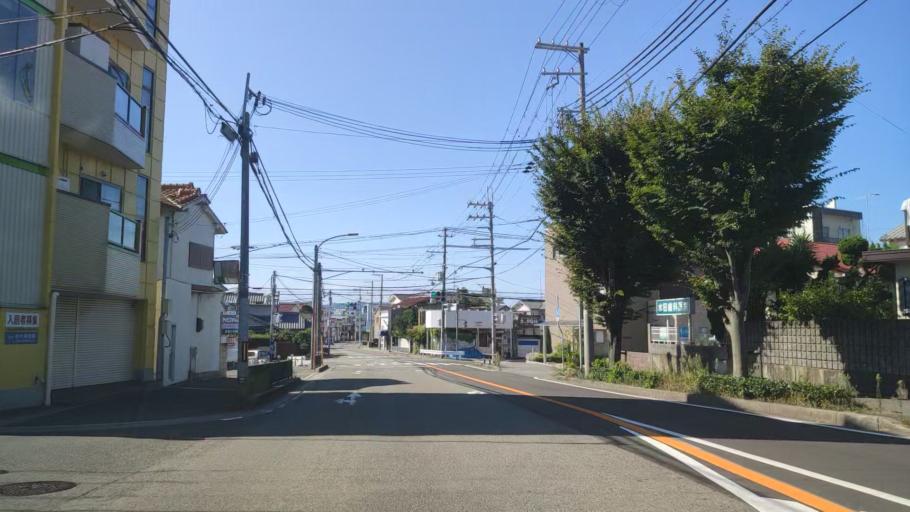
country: JP
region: Hyogo
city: Akashi
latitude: 34.6563
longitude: 135.0081
